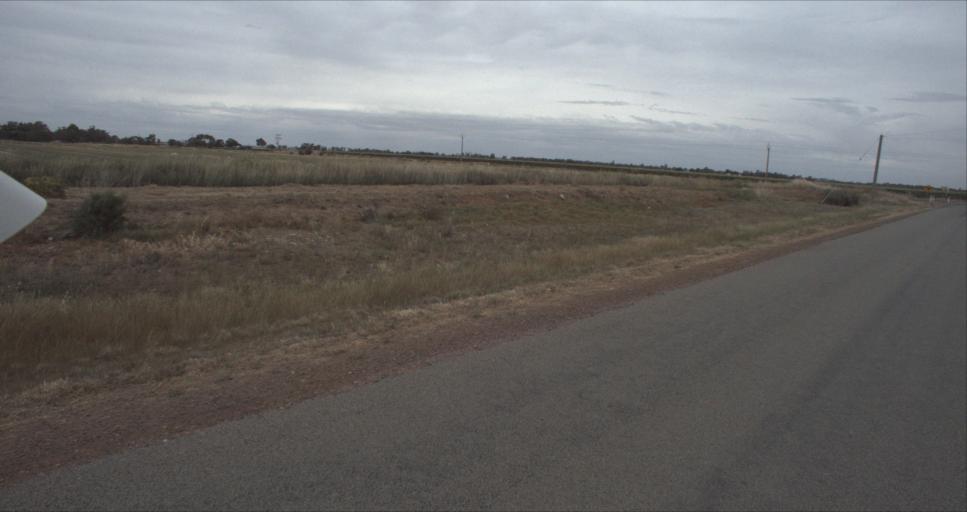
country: AU
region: New South Wales
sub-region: Leeton
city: Leeton
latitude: -34.4998
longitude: 146.3999
